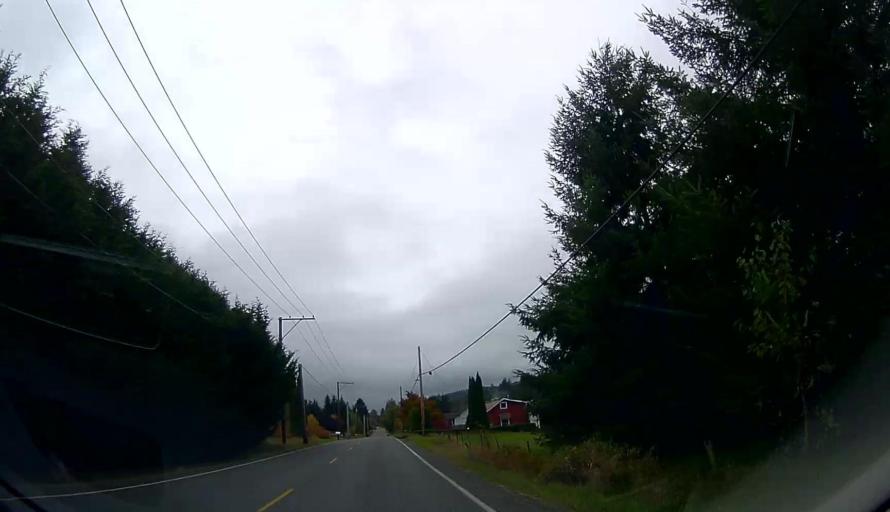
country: US
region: Washington
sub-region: Skagit County
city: Sedro-Woolley
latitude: 48.5271
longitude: -122.0768
